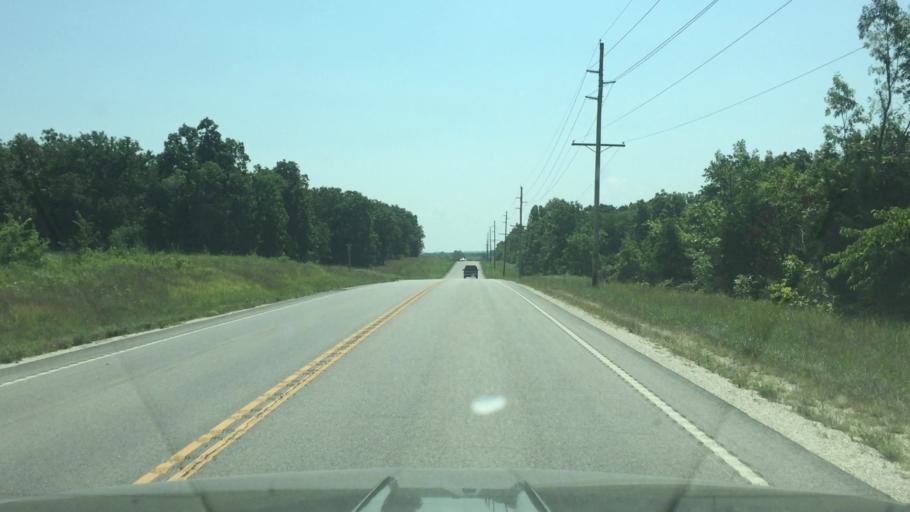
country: US
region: Missouri
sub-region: Miller County
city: Eldon
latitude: 38.3881
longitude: -92.6982
